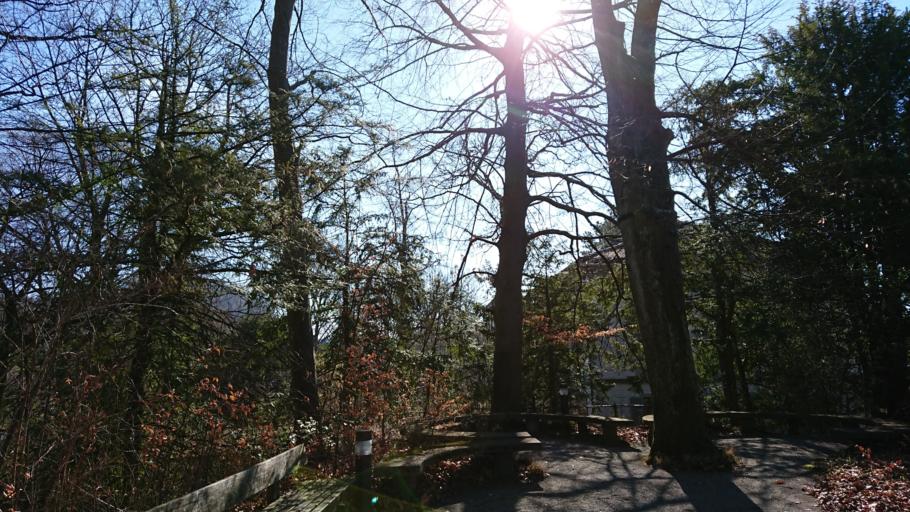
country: CH
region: Zurich
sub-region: Bezirk Zuerich
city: Zuerich (Kreis 8) / Muehlebach
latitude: 47.3581
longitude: 8.5606
